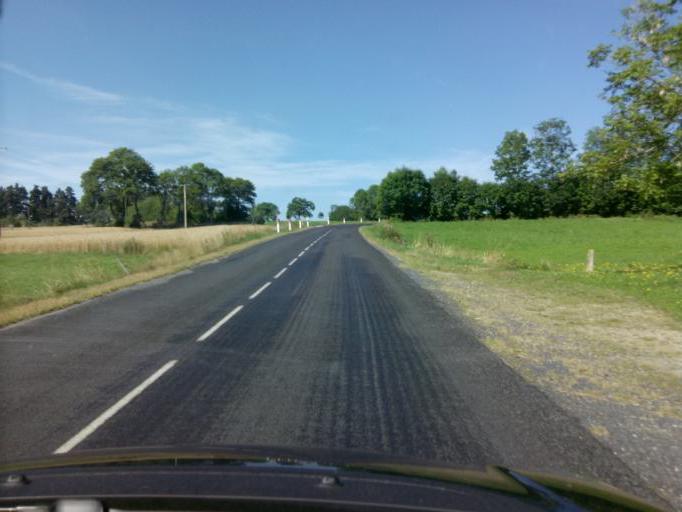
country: FR
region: Rhone-Alpes
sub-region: Departement de la Loire
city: Usson-en-Forez
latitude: 45.3837
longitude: 3.9894
